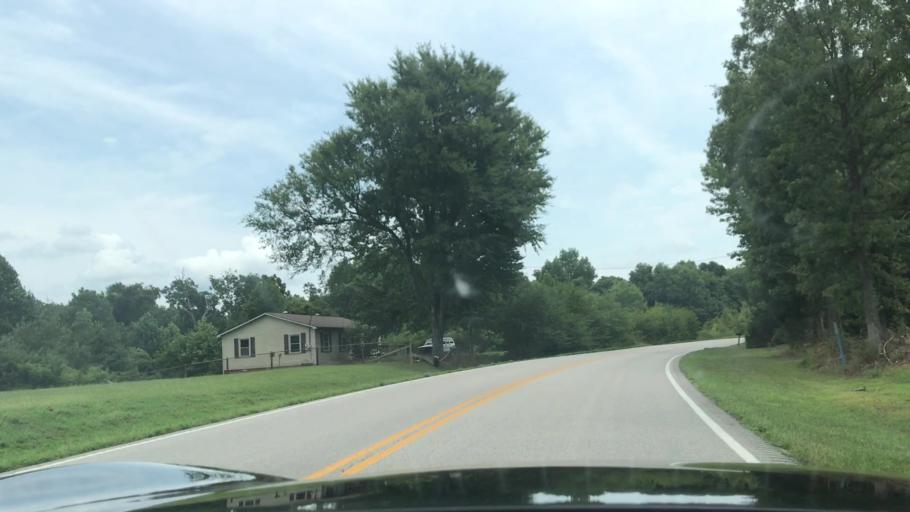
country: US
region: Kentucky
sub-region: Butler County
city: Morgantown
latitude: 37.1820
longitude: -86.8679
